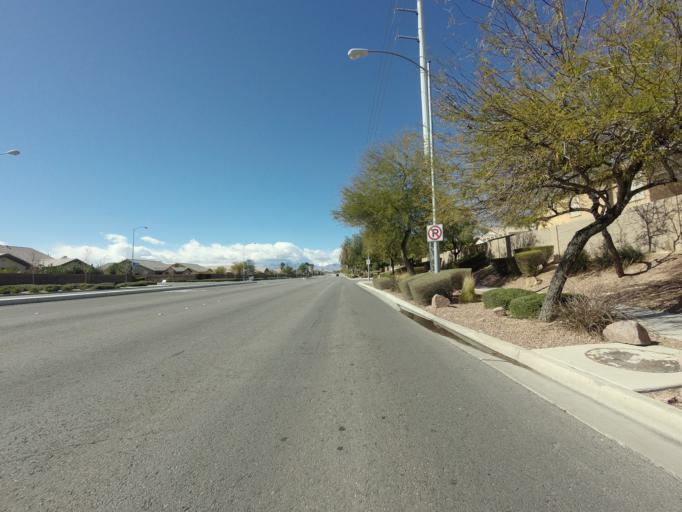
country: US
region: Nevada
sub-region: Clark County
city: Nellis Air Force Base
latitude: 36.2692
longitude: -115.1028
